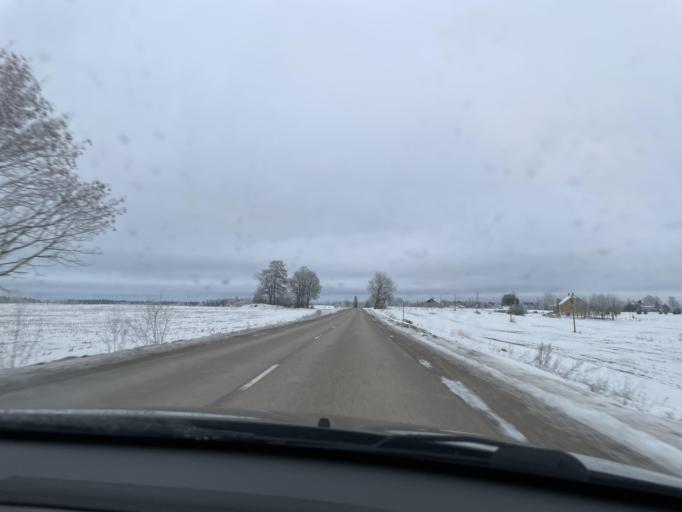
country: LV
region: Rezekne
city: Rezekne
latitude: 56.4977
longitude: 27.4019
